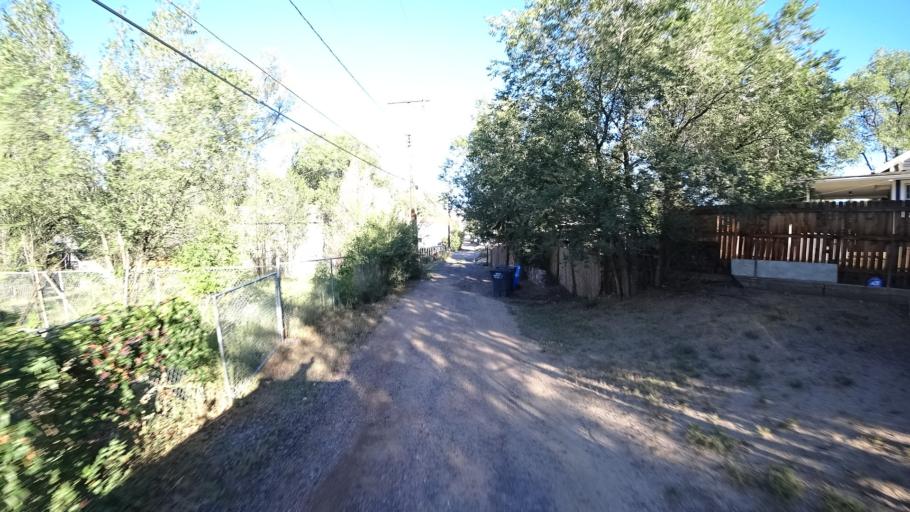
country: US
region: Colorado
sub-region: El Paso County
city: Colorado Springs
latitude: 38.8416
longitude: -104.8450
